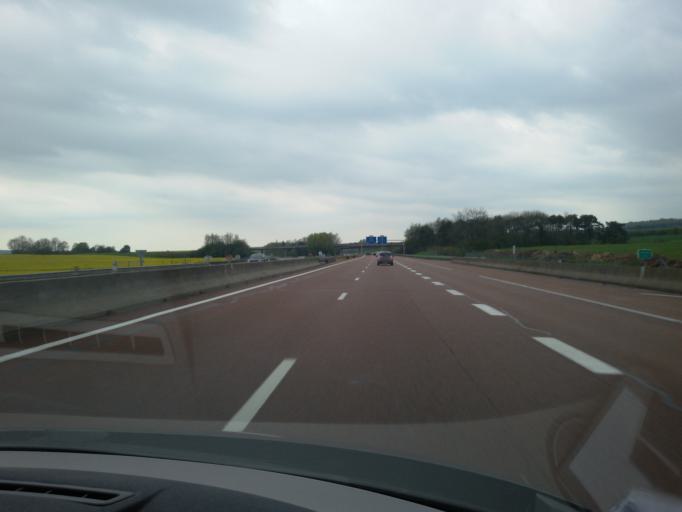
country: FR
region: Champagne-Ardenne
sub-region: Departement de la Haute-Marne
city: Rolampont
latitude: 47.9055
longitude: 5.2233
